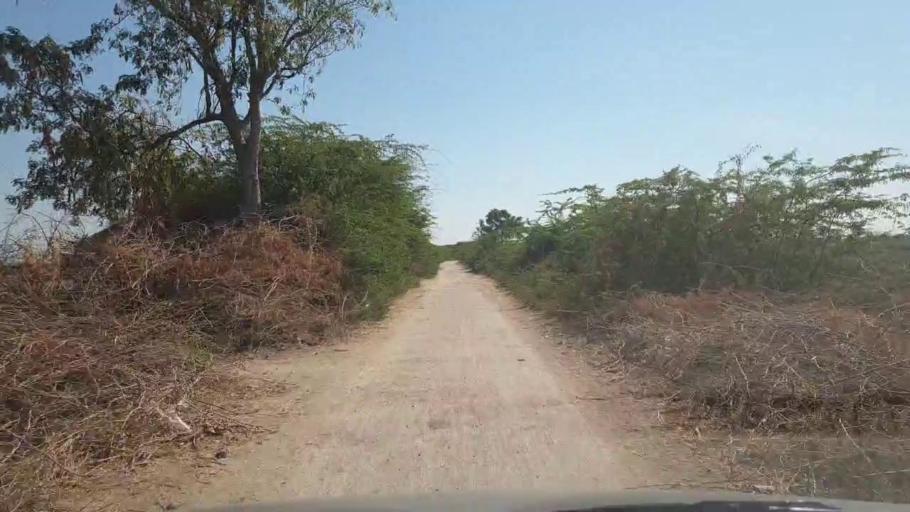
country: PK
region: Sindh
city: Dhoro Naro
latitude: 25.4582
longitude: 69.6042
